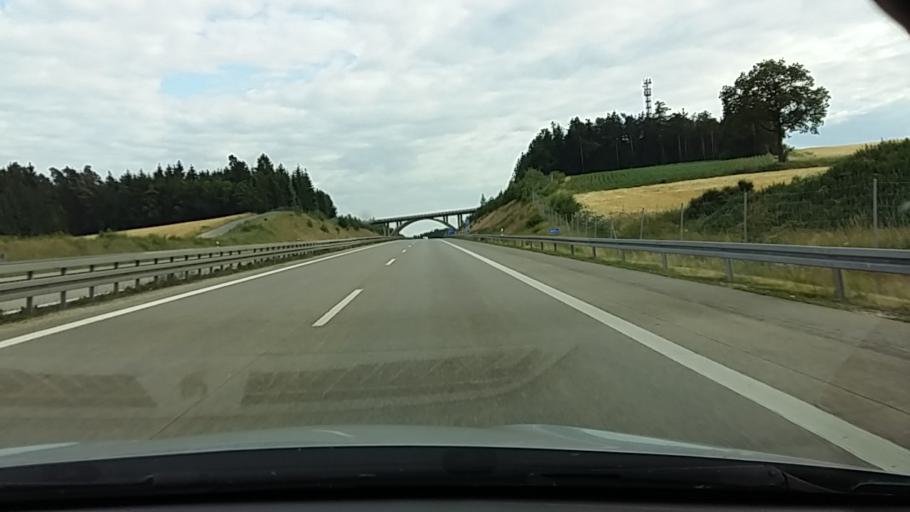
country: DE
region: Bavaria
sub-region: Upper Palatinate
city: Nabburg
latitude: 49.4727
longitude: 12.1349
